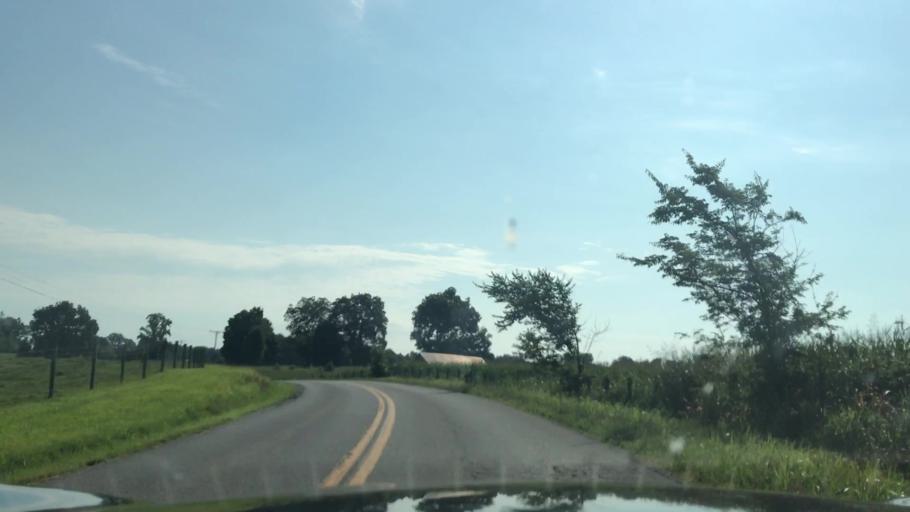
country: US
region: Kentucky
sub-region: Hart County
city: Horse Cave
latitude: 37.1876
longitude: -85.7658
